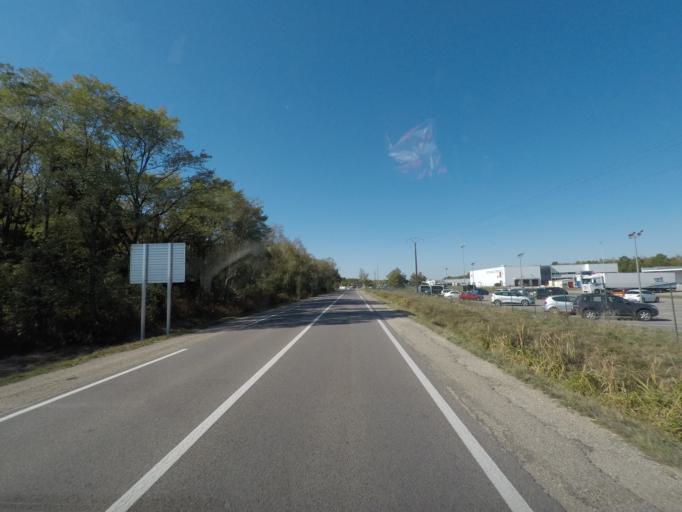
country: FR
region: Rhone-Alpes
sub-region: Departement de l'Ain
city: Attignat
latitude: 46.2595
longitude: 5.1744
